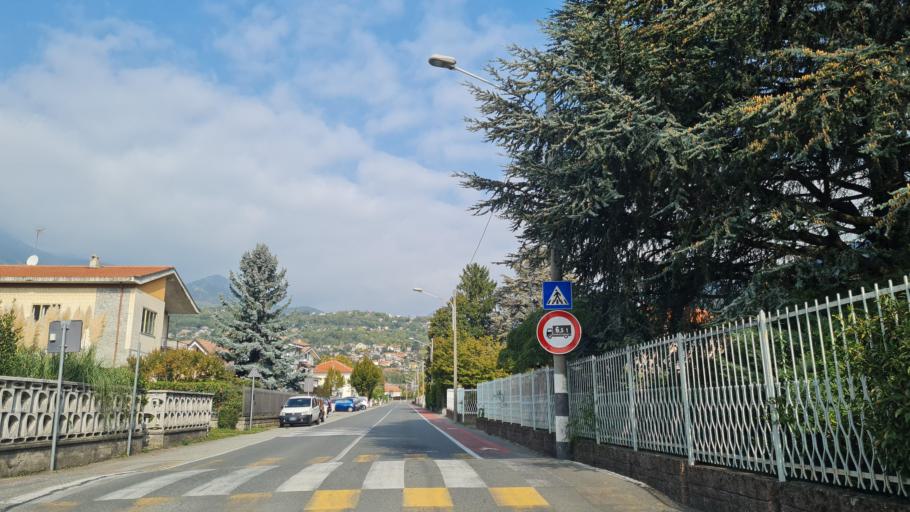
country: IT
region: Piedmont
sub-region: Provincia di Torino
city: Almese-Rivera
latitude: 45.1109
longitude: 7.3991
